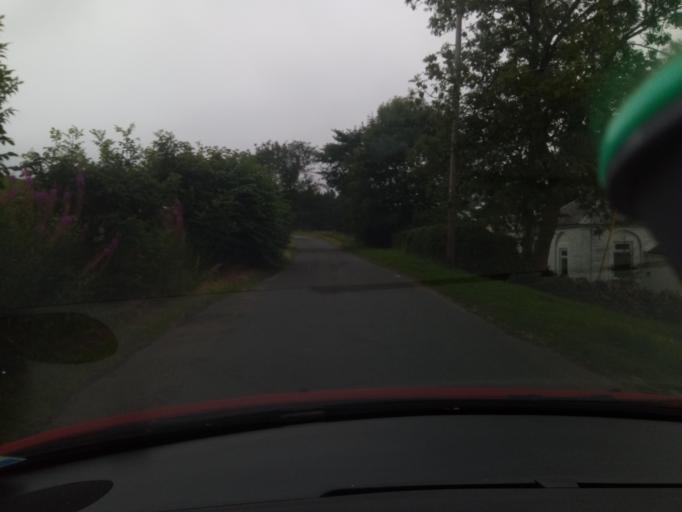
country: GB
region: Scotland
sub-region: The Scottish Borders
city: Galashiels
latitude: 55.7285
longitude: -2.8957
